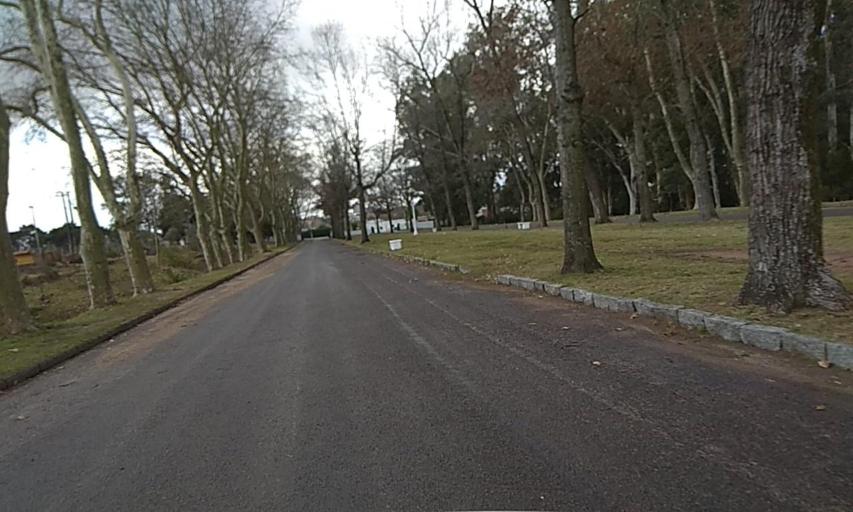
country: UY
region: Florida
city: Florida
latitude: -34.1062
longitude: -56.2260
